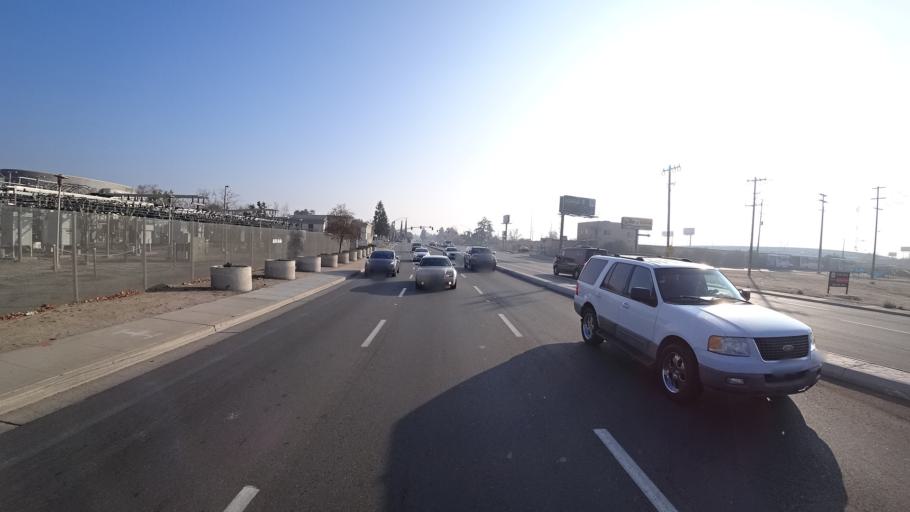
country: US
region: California
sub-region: Kern County
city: Bakersfield
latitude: 35.3736
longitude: -119.0404
